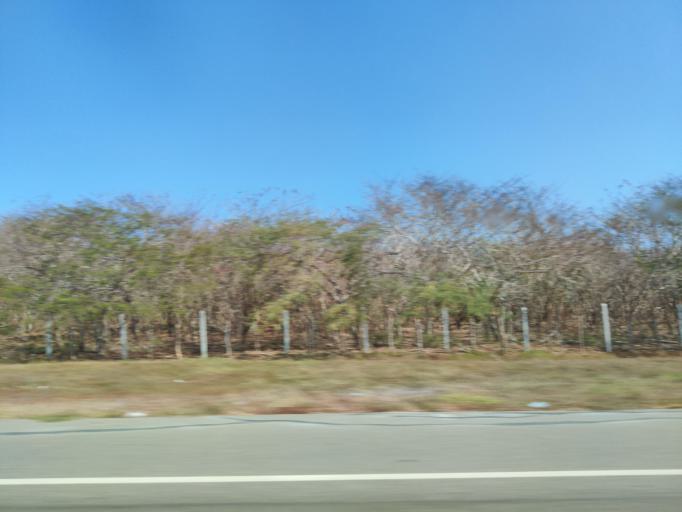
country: CO
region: Atlantico
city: Puerto Colombia
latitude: 10.9683
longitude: -74.9842
